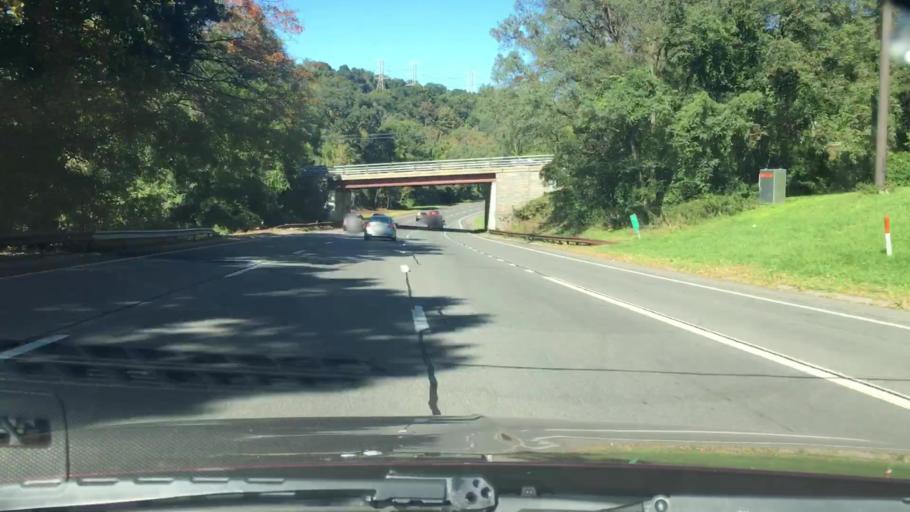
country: US
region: New York
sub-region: Westchester County
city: Greenville
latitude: 40.9874
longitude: -73.8388
